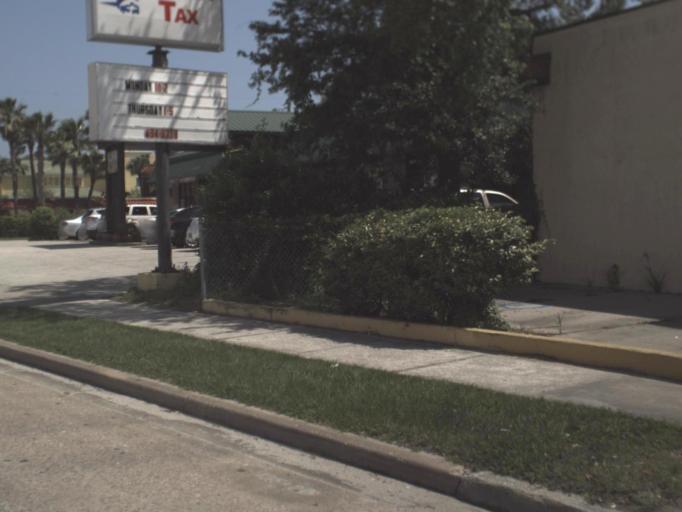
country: US
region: Florida
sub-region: Saint Johns County
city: Saint Augustine
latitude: 29.9033
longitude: -81.3204
